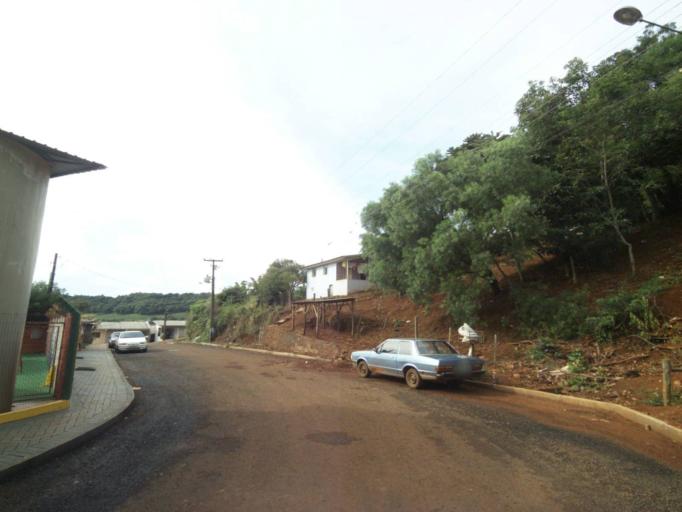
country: BR
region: Parana
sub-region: Guaraniacu
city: Guaraniacu
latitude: -25.1030
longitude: -52.8760
